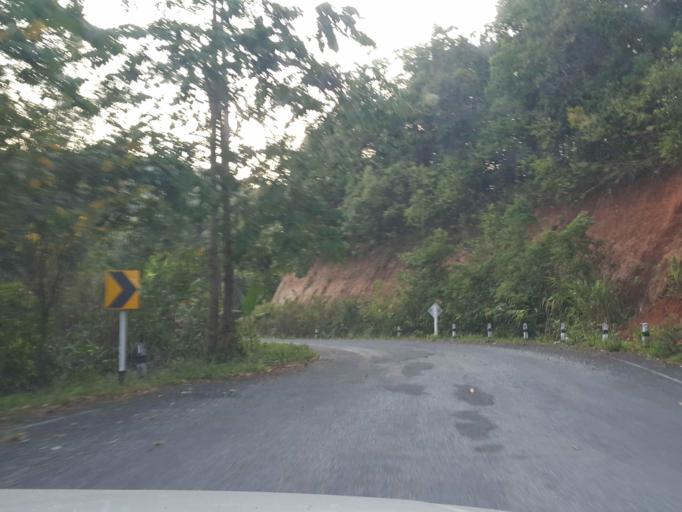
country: TH
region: Chiang Mai
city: Mae On
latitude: 18.9933
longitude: 99.3408
